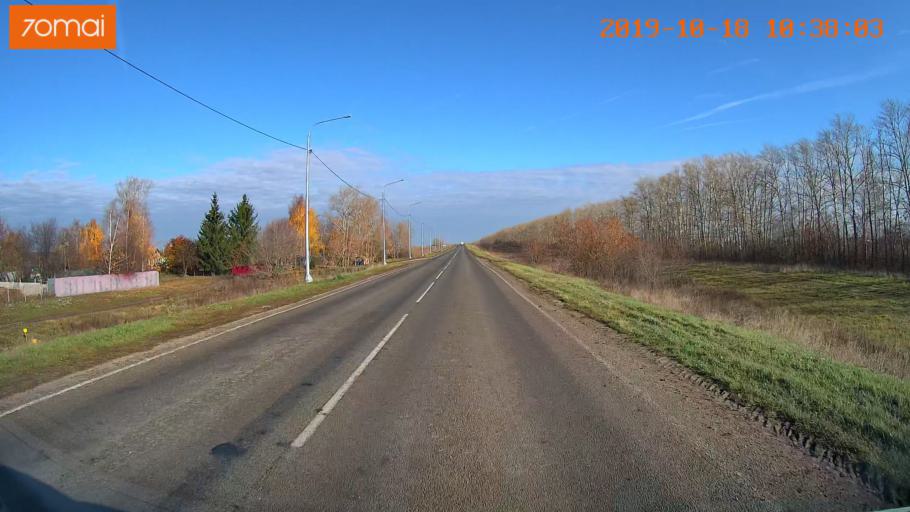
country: RU
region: Tula
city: Kurkino
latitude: 53.5681
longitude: 38.6374
